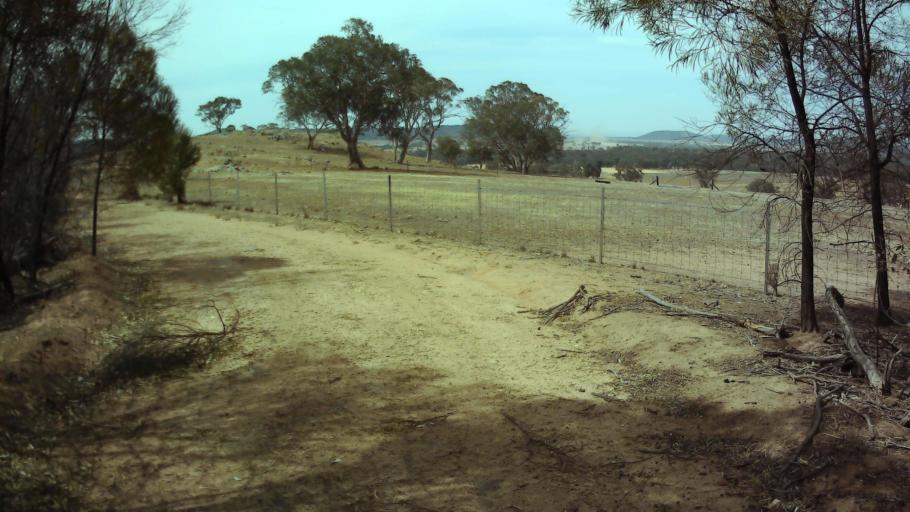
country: AU
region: New South Wales
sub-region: Weddin
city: Grenfell
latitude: -33.8663
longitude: 148.1663
